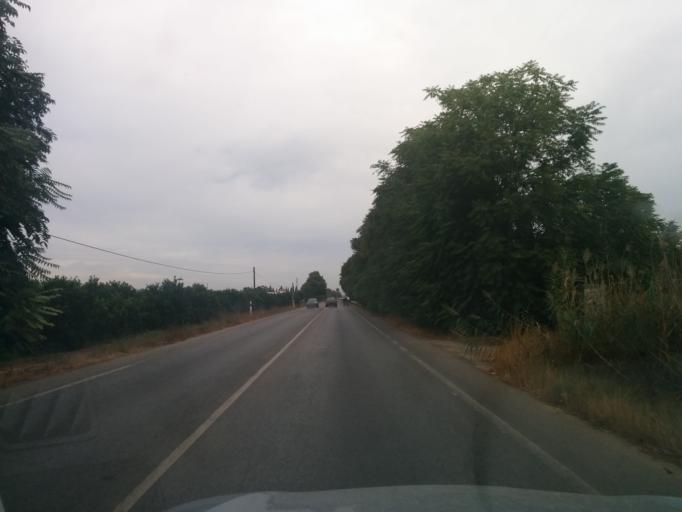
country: ES
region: Andalusia
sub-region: Provincia de Sevilla
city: La Algaba
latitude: 37.4735
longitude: -6.0095
